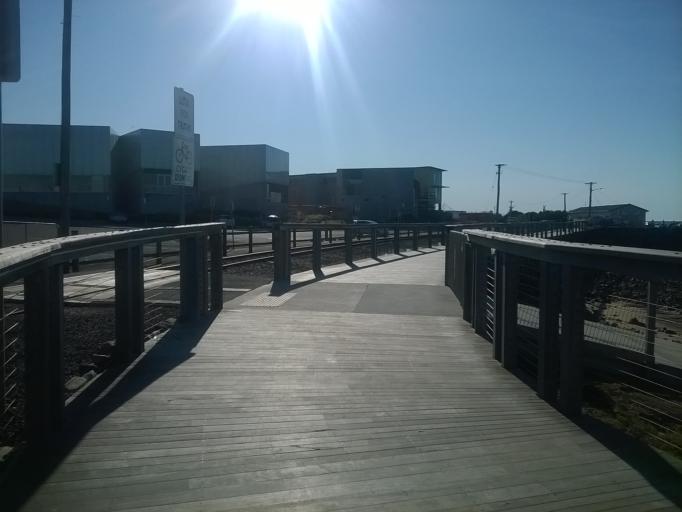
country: AU
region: Tasmania
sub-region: Burnie
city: Burnie
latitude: -41.0473
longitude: 145.9015
